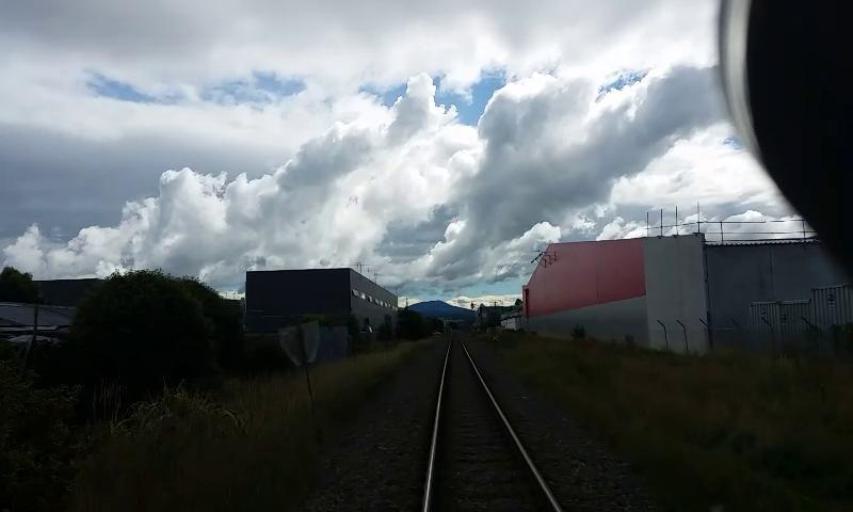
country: NZ
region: Canterbury
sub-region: Waimakariri District
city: Woodend
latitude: -43.3050
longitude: 172.5987
